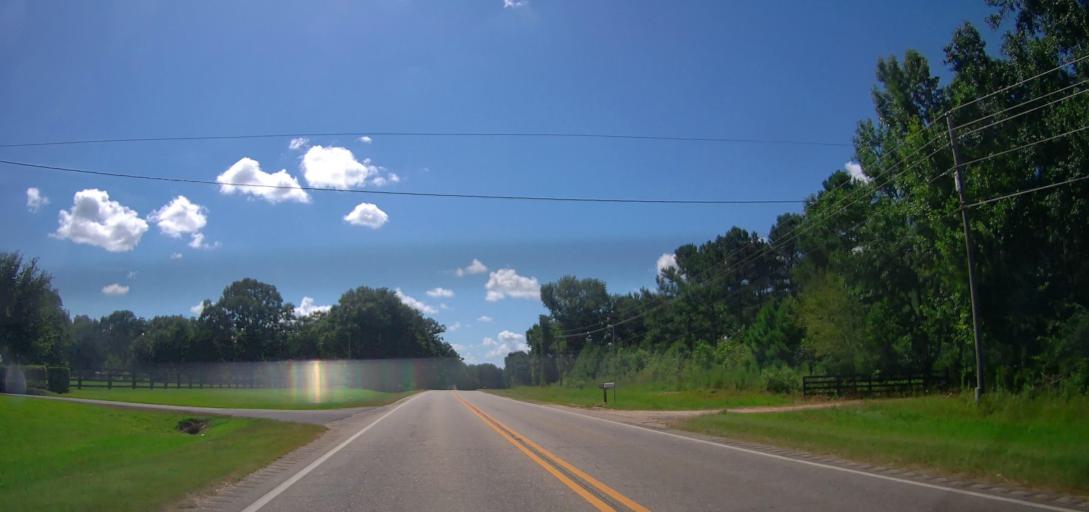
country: US
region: Alabama
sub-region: Elmore County
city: Tallassee
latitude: 32.3799
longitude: -85.8698
